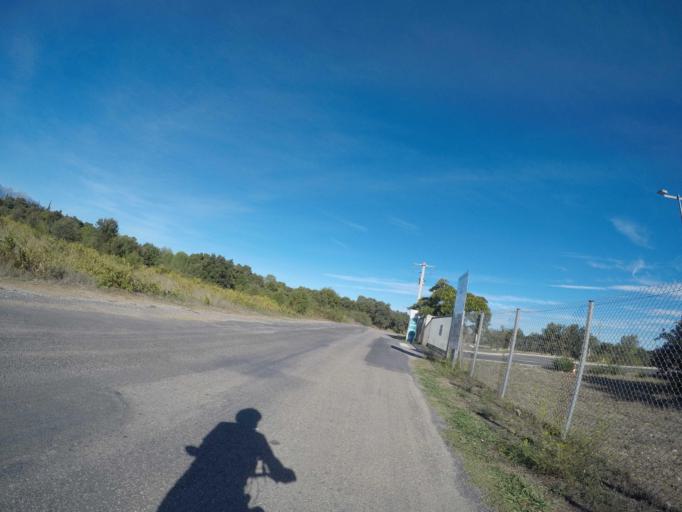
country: FR
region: Languedoc-Roussillon
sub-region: Departement des Pyrenees-Orientales
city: Trouillas
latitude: 42.5902
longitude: 2.8076
